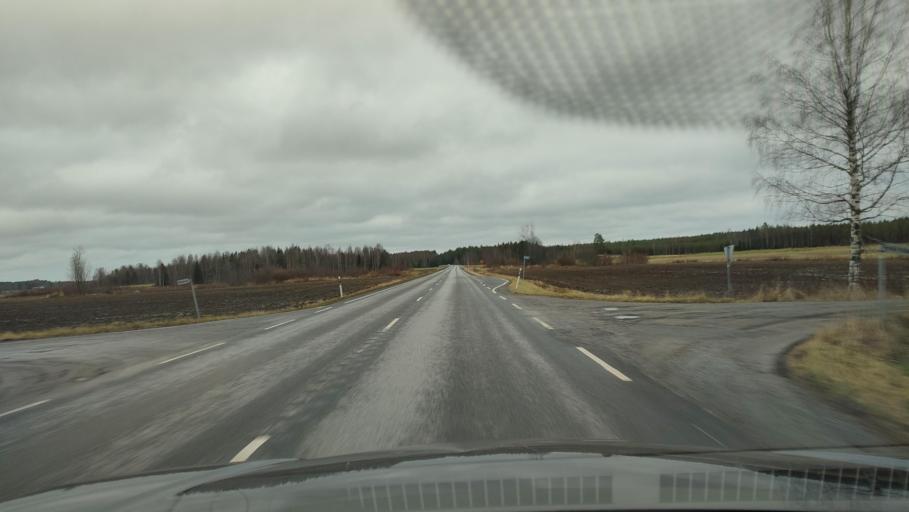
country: FI
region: Southern Ostrobothnia
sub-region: Suupohja
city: Kauhajoki
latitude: 62.4841
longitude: 22.2853
